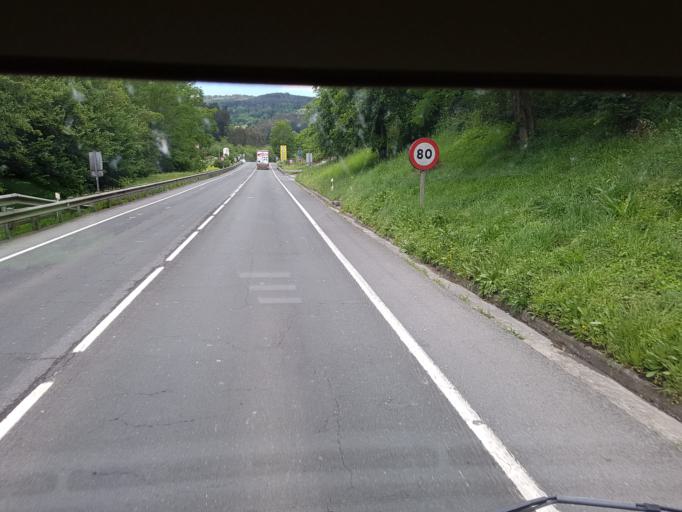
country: ES
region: Basque Country
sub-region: Bizkaia
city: Galdakao
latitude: 43.2326
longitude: -2.7945
